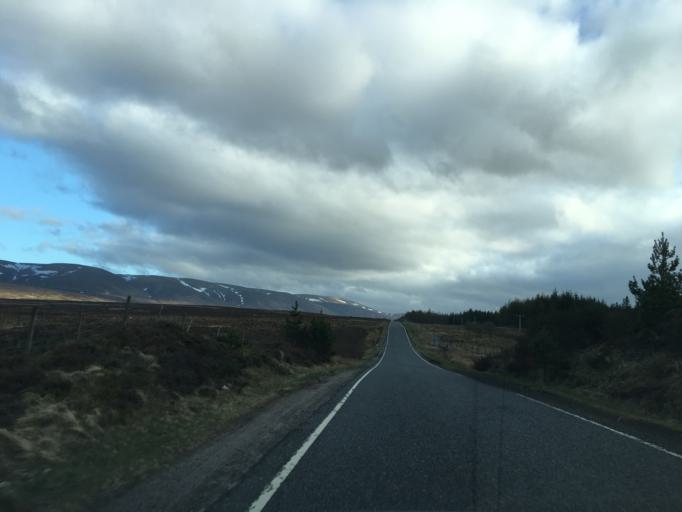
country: GB
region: Scotland
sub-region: Highland
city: Kingussie
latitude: 56.9571
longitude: -4.2445
